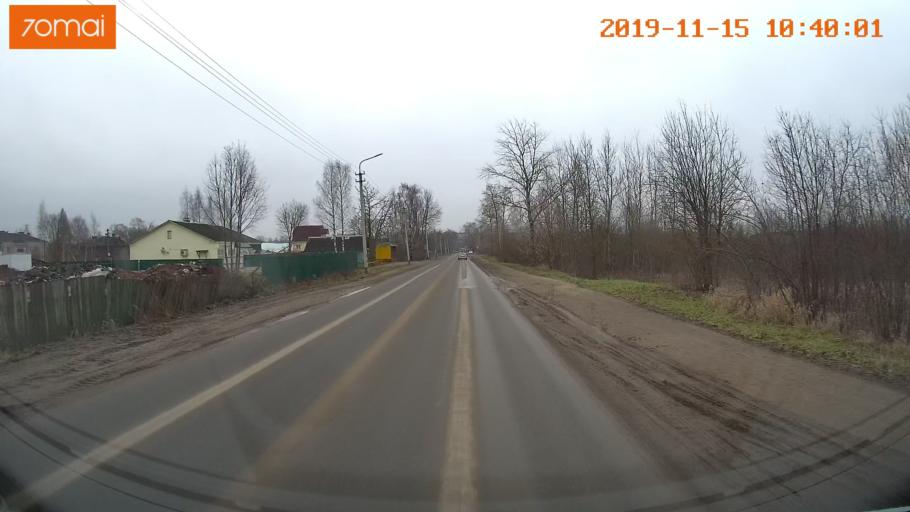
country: RU
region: Vologda
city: Sheksna
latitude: 59.2173
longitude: 38.5104
